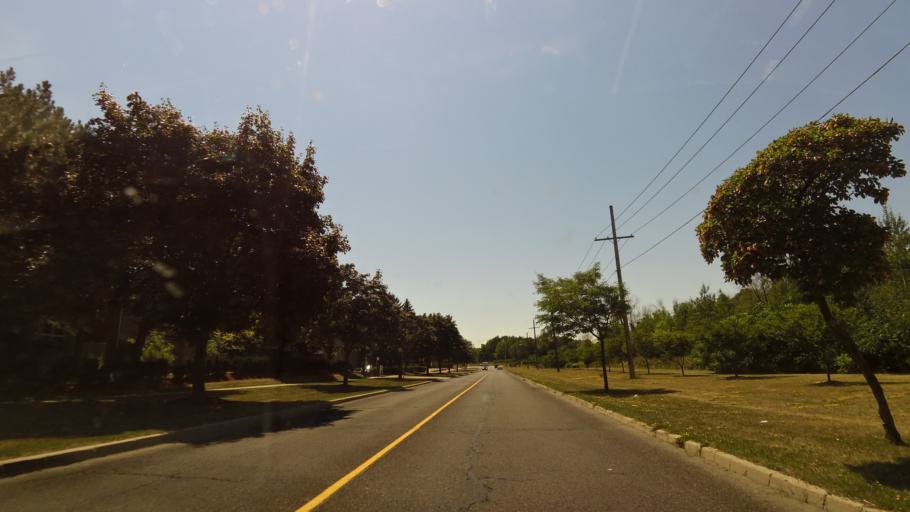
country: CA
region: Ontario
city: Etobicoke
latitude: 43.6470
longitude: -79.5877
